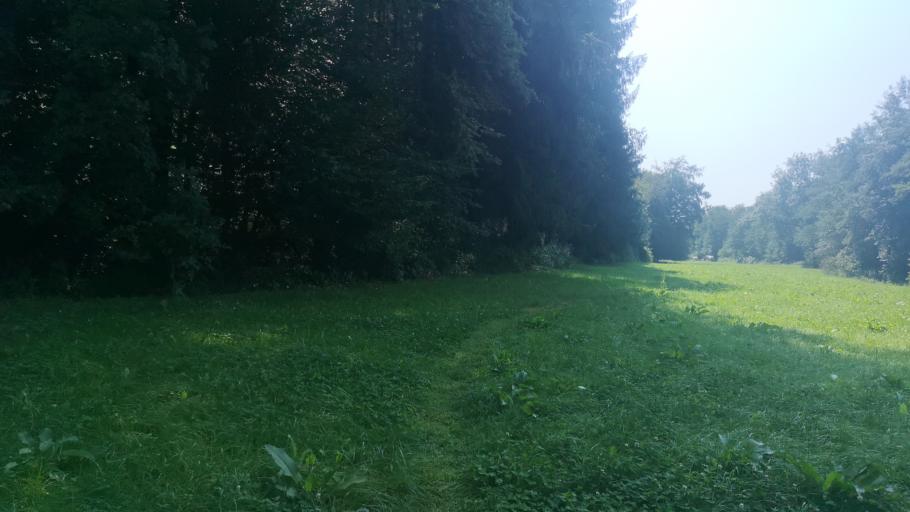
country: AT
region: Styria
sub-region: Politischer Bezirk Deutschlandsberg
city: Lannach
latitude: 46.9382
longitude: 15.3384
